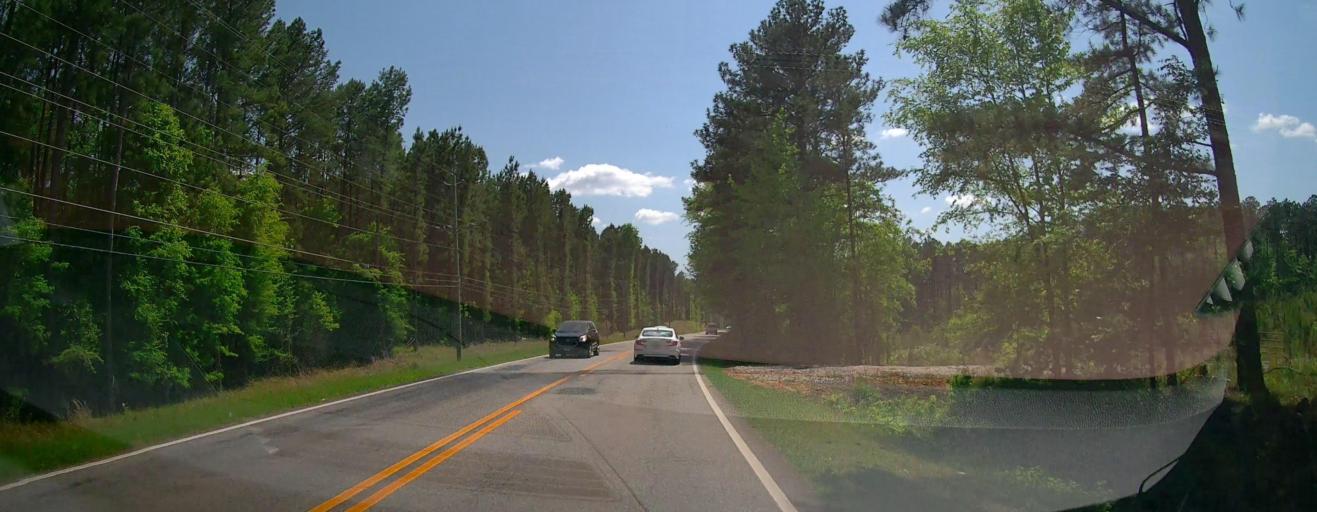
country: US
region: Georgia
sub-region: Putnam County
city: Eatonton
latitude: 33.2456
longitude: -83.3041
